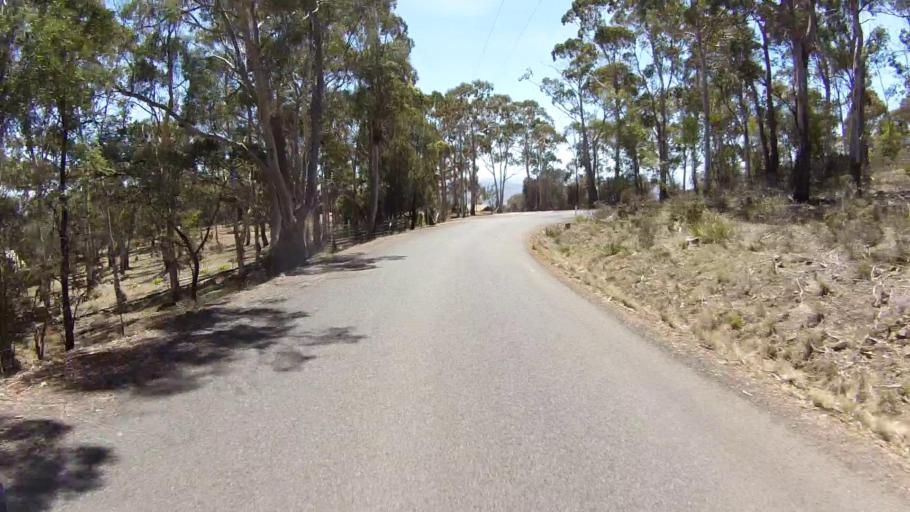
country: AU
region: Tasmania
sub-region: Clarence
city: Cambridge
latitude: -42.8463
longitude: 147.4315
